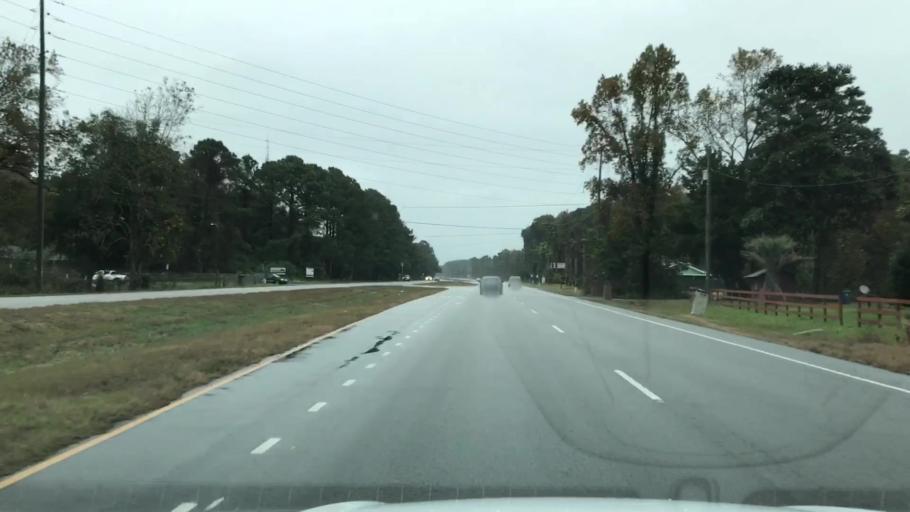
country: US
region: South Carolina
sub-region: Charleston County
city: Isle of Palms
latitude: 32.8951
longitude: -79.7358
